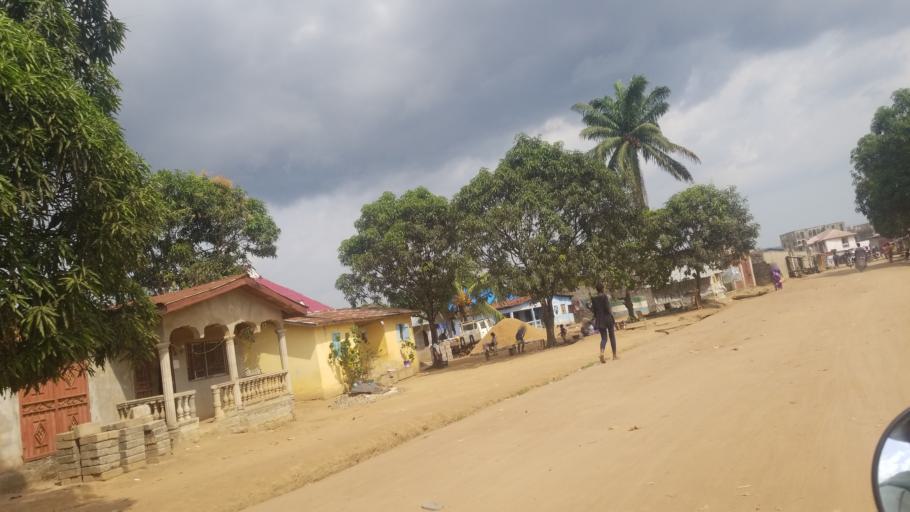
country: SL
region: Western Area
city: Waterloo
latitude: 8.3334
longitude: -13.0490
